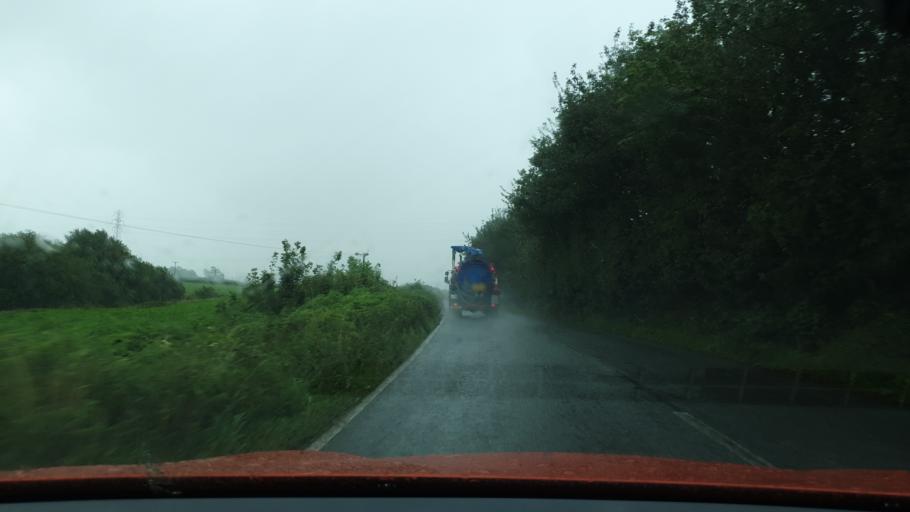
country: GB
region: England
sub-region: Cumbria
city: Askam in Furness
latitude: 54.2593
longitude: -3.2072
